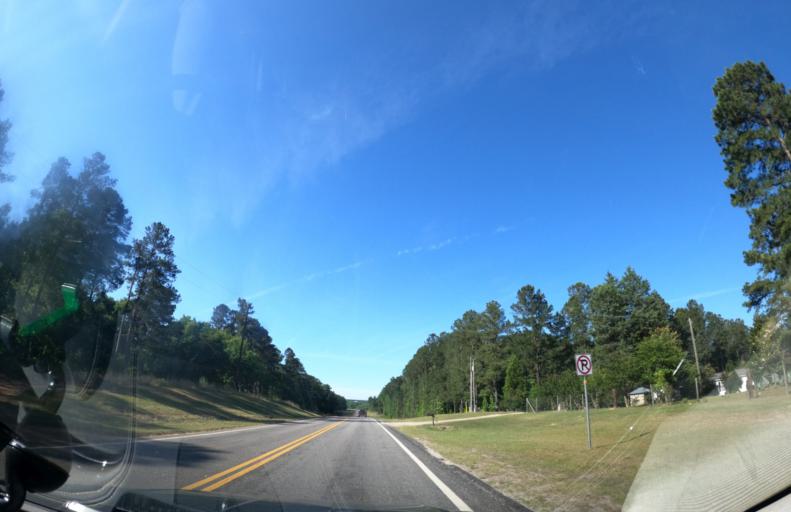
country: US
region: Georgia
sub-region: Columbia County
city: Harlem
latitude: 33.3222
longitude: -82.3721
